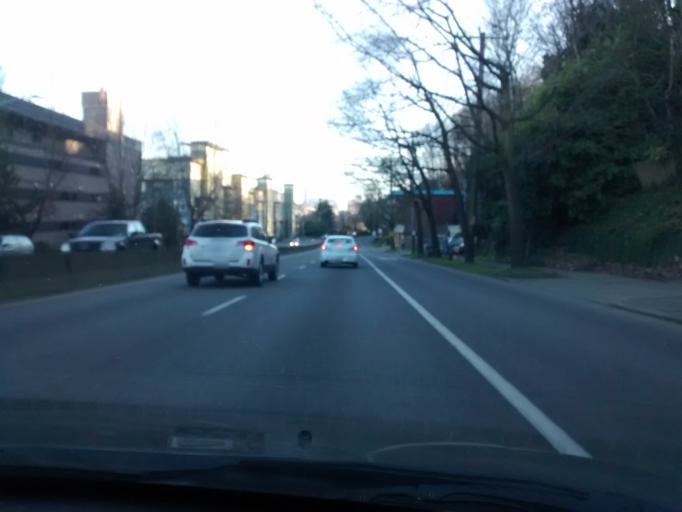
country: US
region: Washington
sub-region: King County
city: Seattle
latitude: 47.6381
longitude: -122.3450
